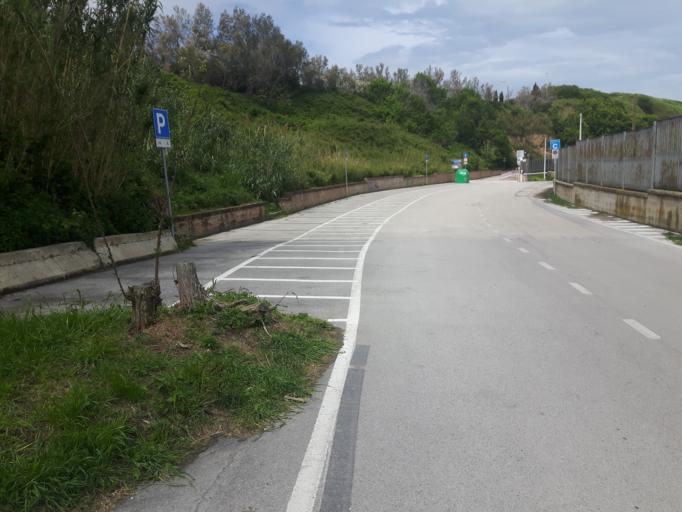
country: IT
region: Abruzzo
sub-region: Provincia di Chieti
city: Vasto
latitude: 42.1712
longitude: 14.7111
